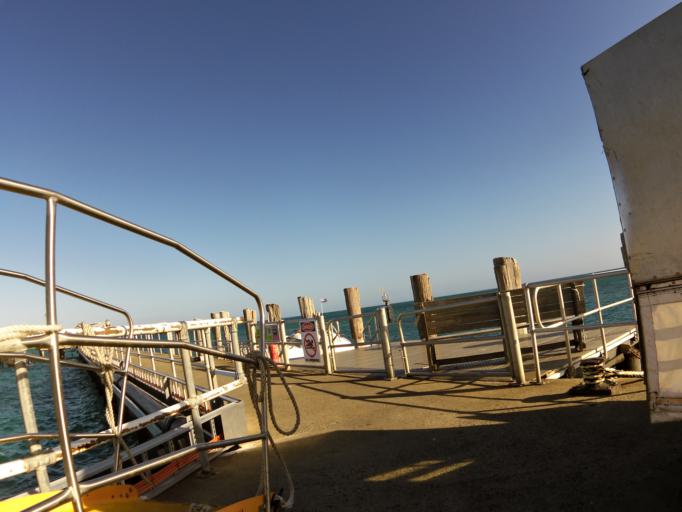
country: AU
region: Queensland
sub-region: Cairns
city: Yorkeys Knob
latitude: -16.7580
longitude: 145.9702
